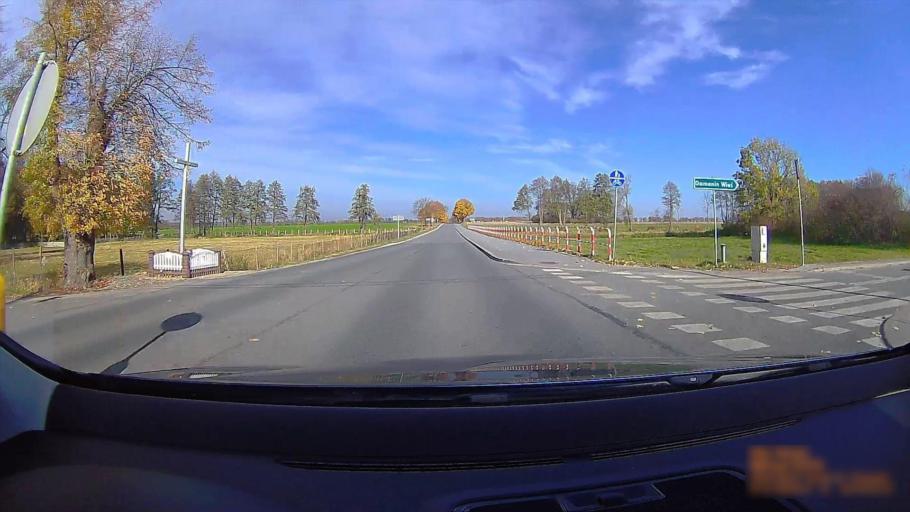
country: PL
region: Greater Poland Voivodeship
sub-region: Powiat kepinski
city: Kepno
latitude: 51.3452
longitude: 18.0243
